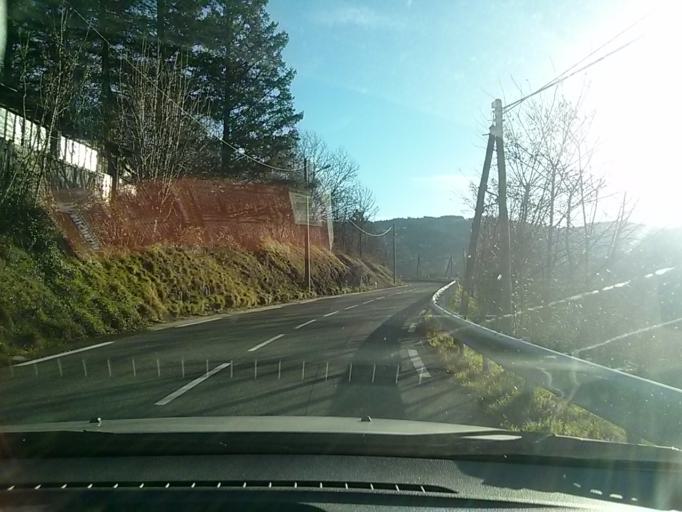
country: FR
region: Rhone-Alpes
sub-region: Departement de la Loire
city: Saint-Jean-Bonnefonds
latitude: 45.4111
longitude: 4.4336
